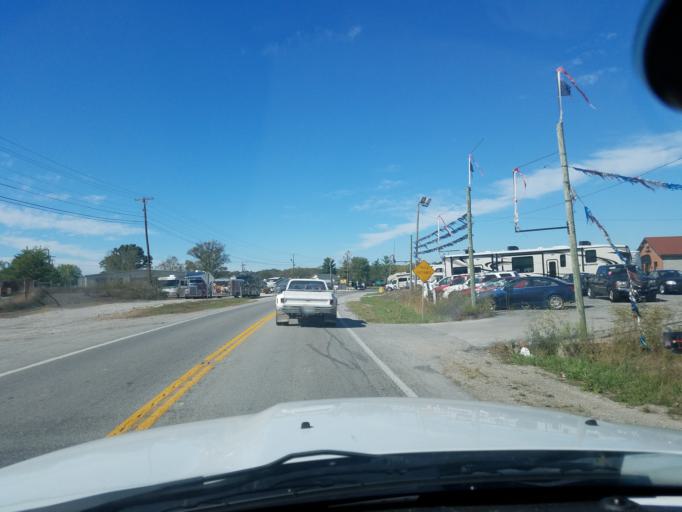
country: US
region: Kentucky
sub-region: Laurel County
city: London
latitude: 37.0641
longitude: -84.0566
